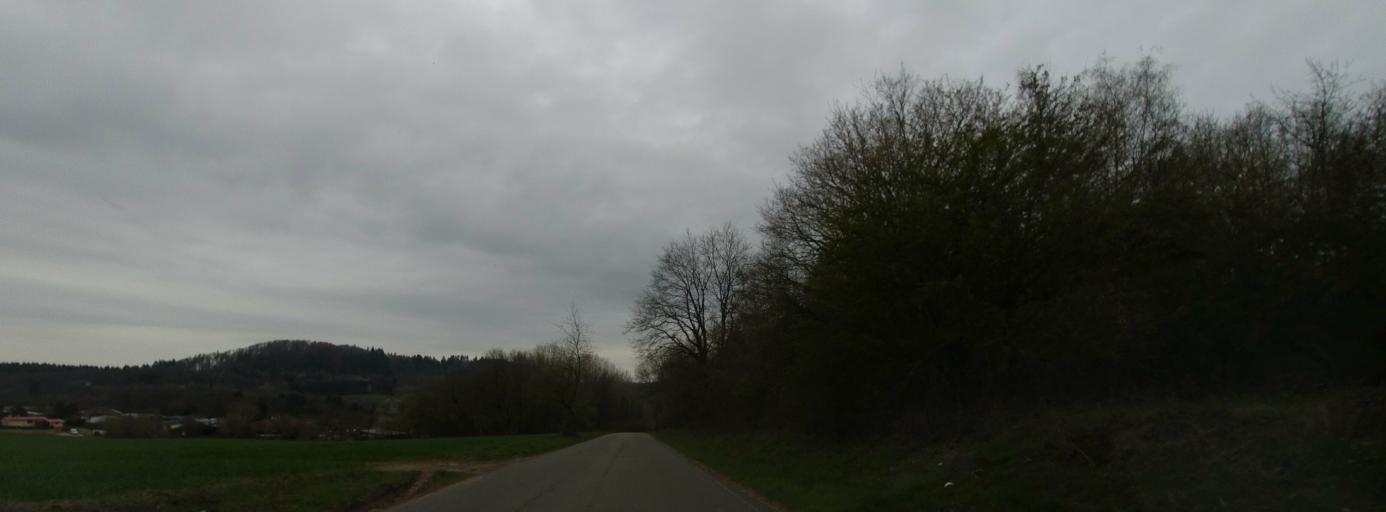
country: DE
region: Saarland
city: Nalbach
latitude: 49.4349
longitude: 6.7519
